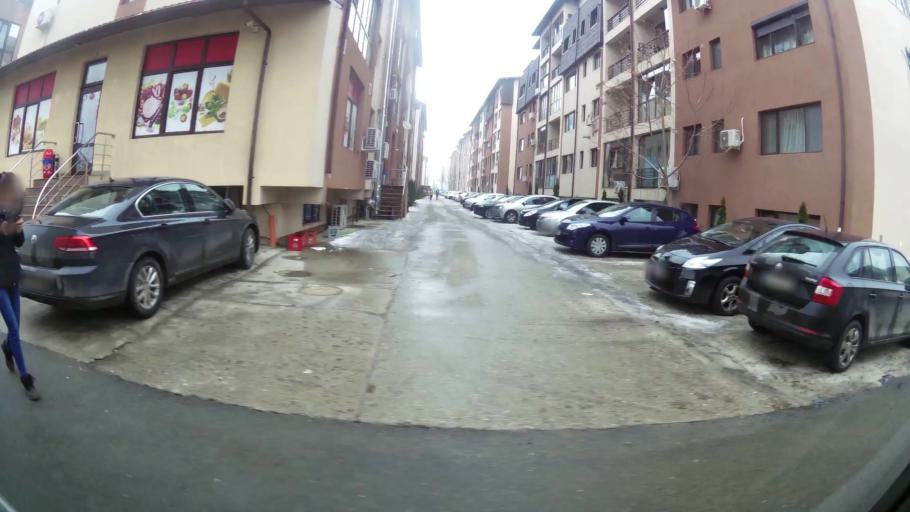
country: RO
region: Ilfov
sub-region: Comuna Chiajna
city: Rosu
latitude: 44.4439
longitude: 26.0070
